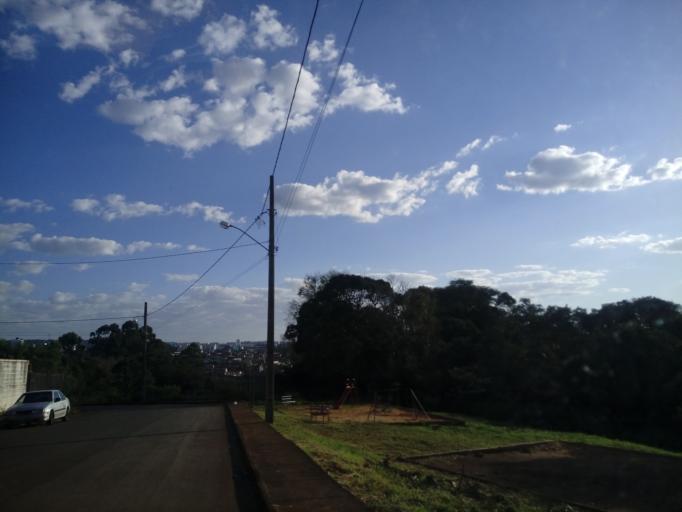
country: BR
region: Santa Catarina
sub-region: Chapeco
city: Chapeco
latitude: -27.1092
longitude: -52.6676
